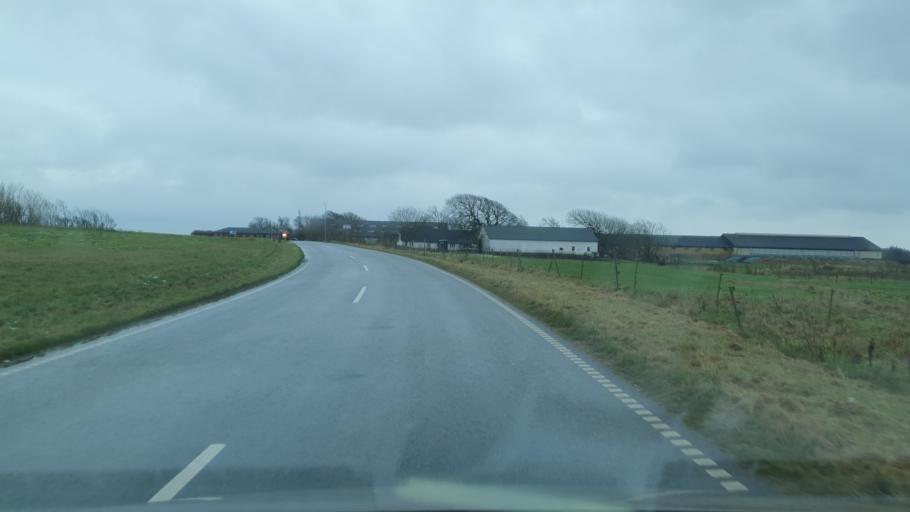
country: DK
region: North Denmark
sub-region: Jammerbugt Kommune
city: Fjerritslev
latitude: 57.1128
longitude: 9.1279
